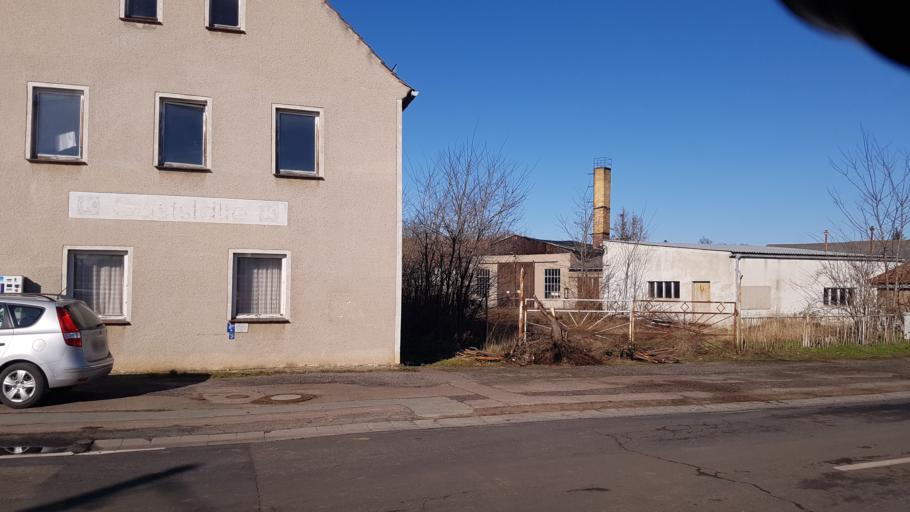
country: DE
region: Saxony
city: Arzberg
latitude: 51.5170
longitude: 13.1853
